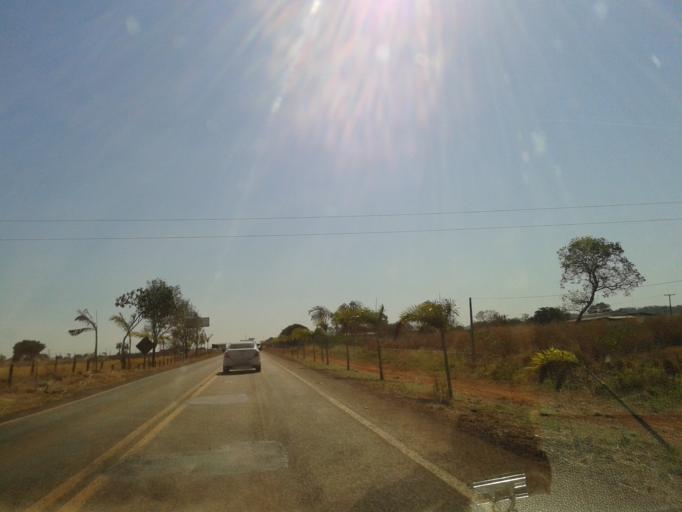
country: BR
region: Goias
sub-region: Crixas
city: Crixas
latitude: -14.1183
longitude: -50.3457
